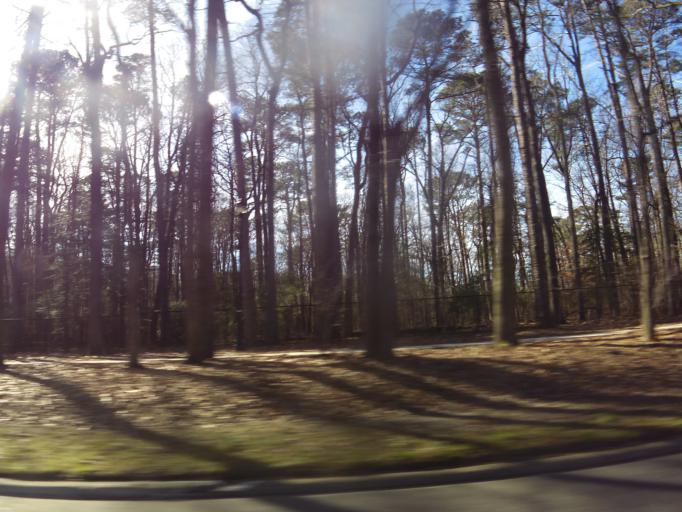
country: US
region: Virginia
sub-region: City of Newport News
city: Newport News
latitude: 37.0541
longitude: -76.4804
